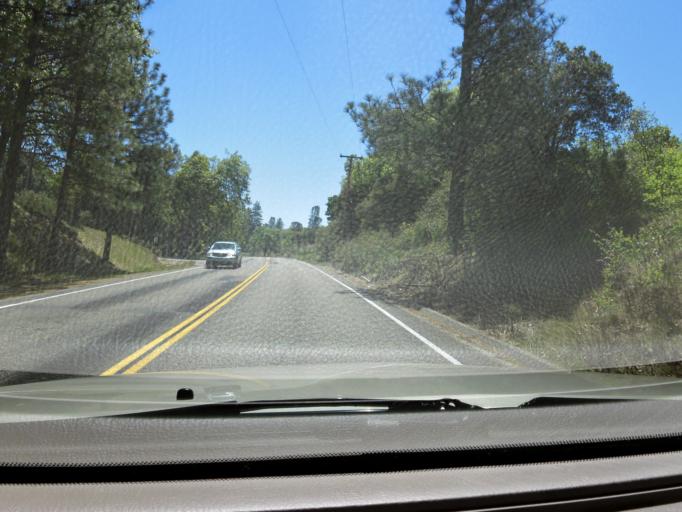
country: US
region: California
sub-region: Madera County
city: Oakhurst
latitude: 37.2681
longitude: -119.5140
